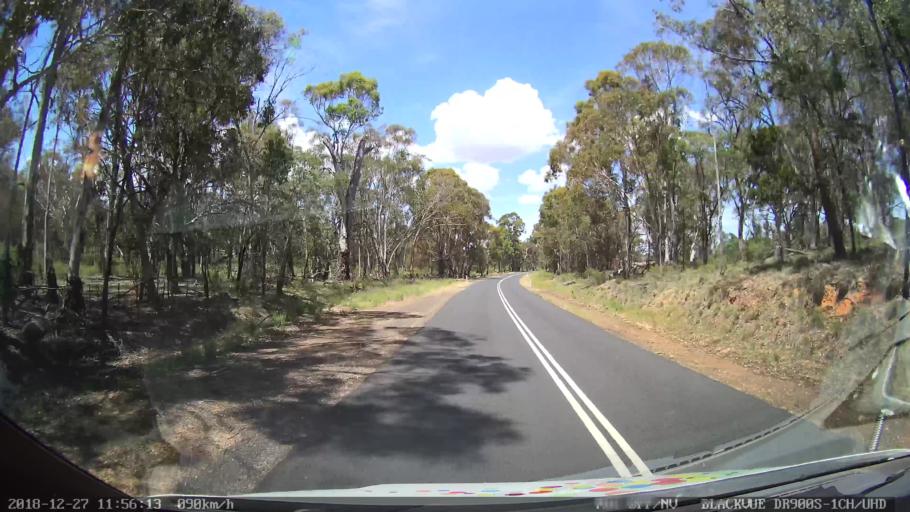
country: AU
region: New South Wales
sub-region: Blayney
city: Blayney
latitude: -33.6960
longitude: 149.3933
